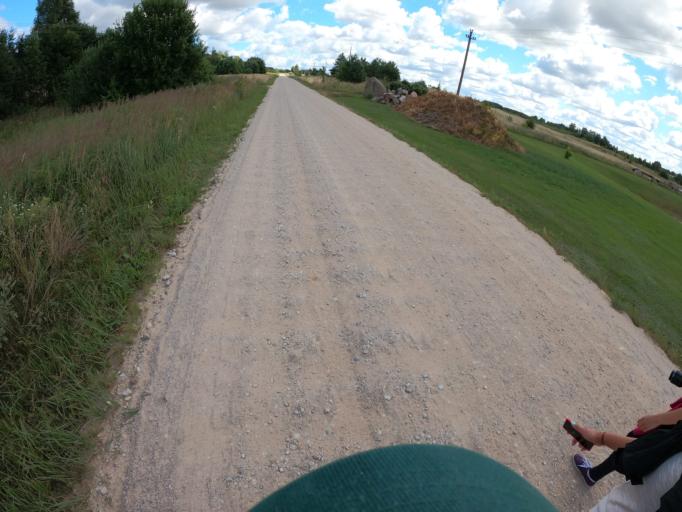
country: LT
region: Alytaus apskritis
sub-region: Alytus
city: Alytus
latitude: 54.3322
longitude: 24.0801
